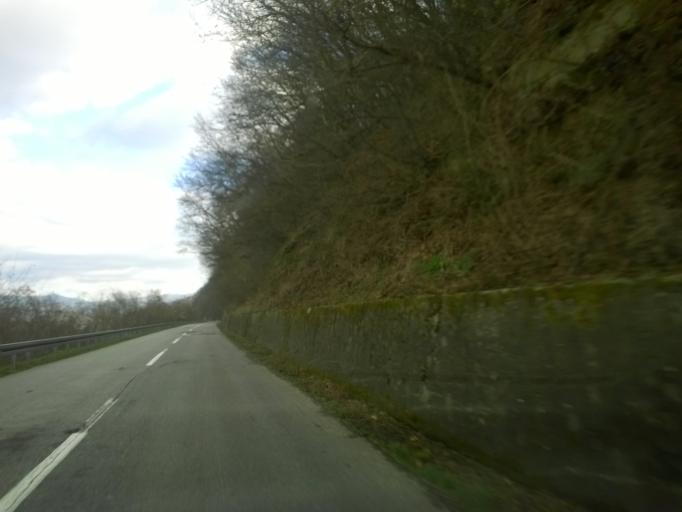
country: RO
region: Caras-Severin
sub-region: Comuna Berzasca
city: Liubcova
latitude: 44.6440
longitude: 21.8804
